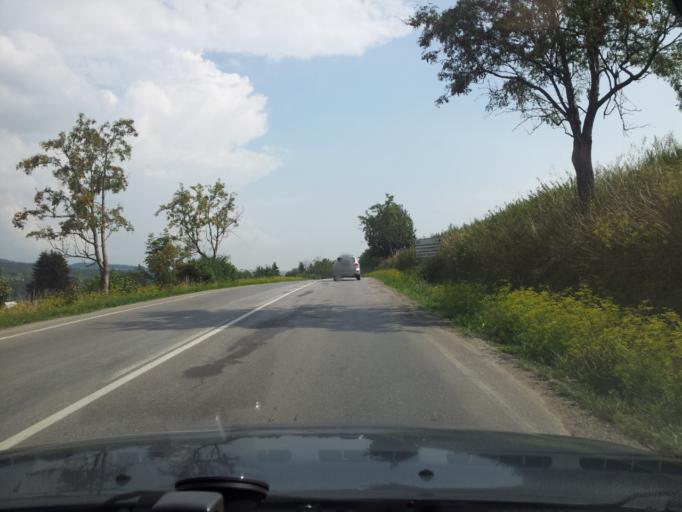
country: SK
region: Zilinsky
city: Namestovo
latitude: 49.3842
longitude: 19.4464
